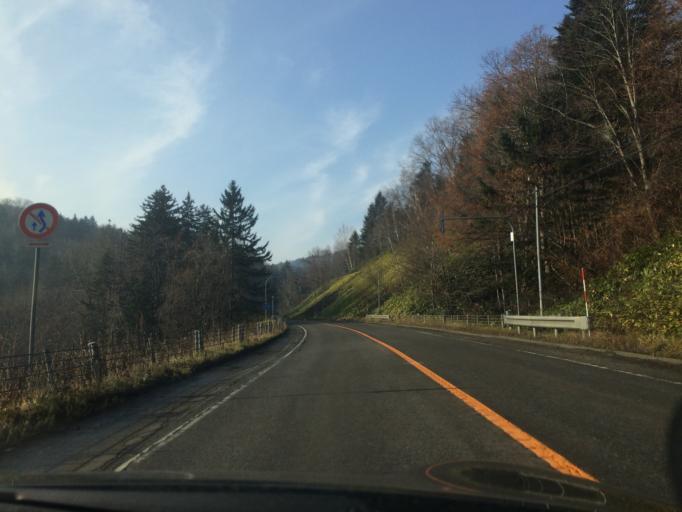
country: JP
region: Hokkaido
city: Shimo-furano
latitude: 42.8801
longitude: 142.2307
